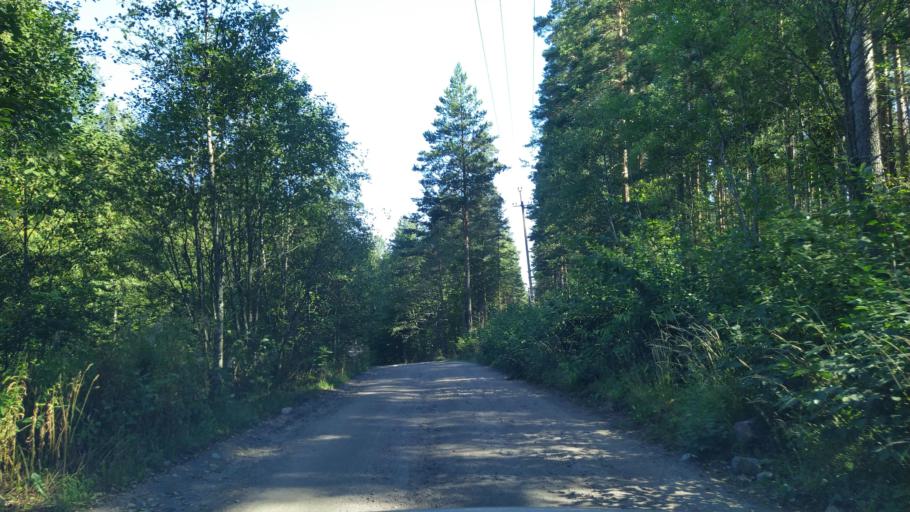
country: RU
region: Leningrad
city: Priozersk
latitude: 60.9715
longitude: 30.3021
